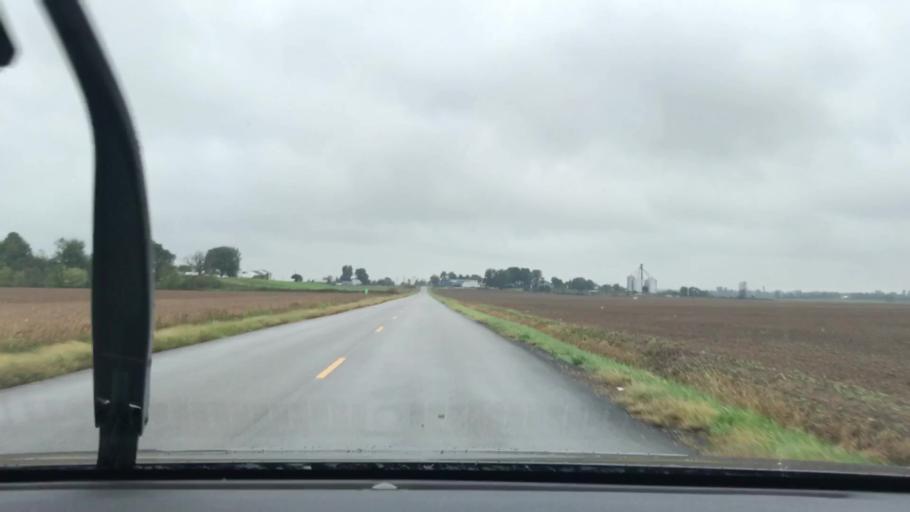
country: US
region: Kentucky
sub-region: Hopkins County
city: Madisonville
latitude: 37.3786
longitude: -87.3449
